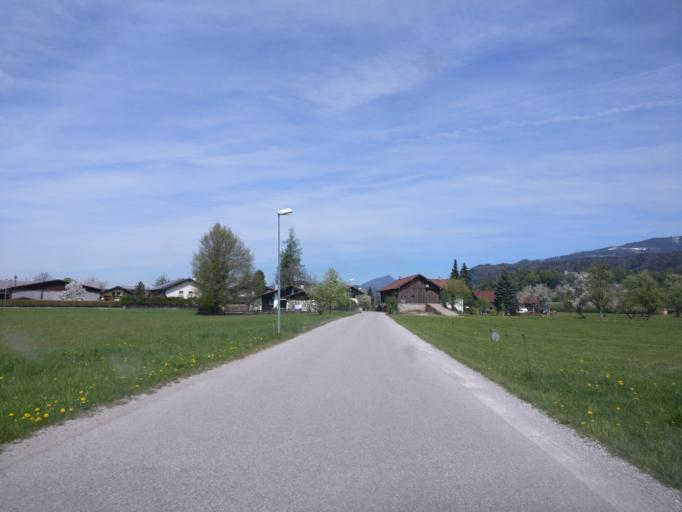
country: AT
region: Salzburg
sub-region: Politischer Bezirk Hallein
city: Kuchl
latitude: 47.6252
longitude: 13.1549
